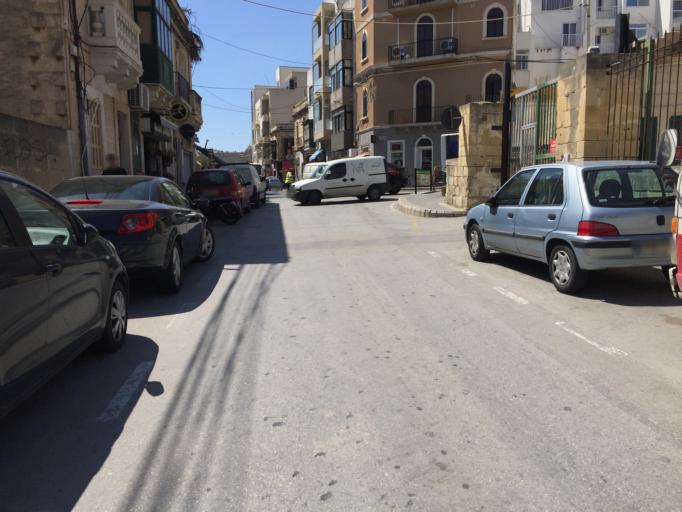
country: MT
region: Saint Julian
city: San Giljan
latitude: 35.9224
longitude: 14.4900
